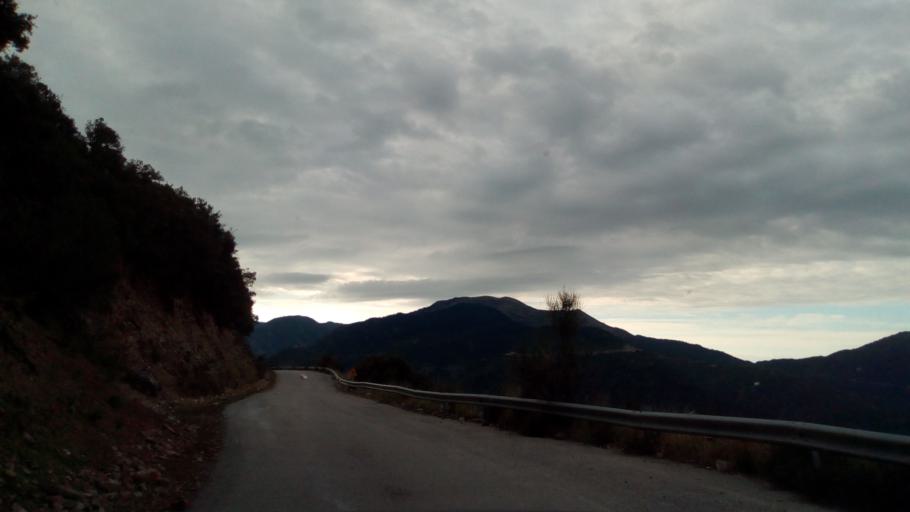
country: GR
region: West Greece
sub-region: Nomos Aitolias kai Akarnanias
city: Thermo
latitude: 38.5990
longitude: 21.8083
